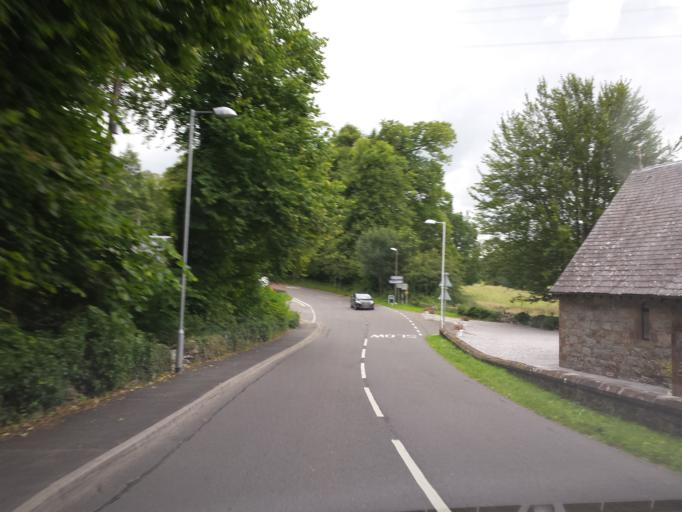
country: GB
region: Scotland
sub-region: Dumfries and Galloway
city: Dumfries
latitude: 54.9805
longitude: -3.6231
